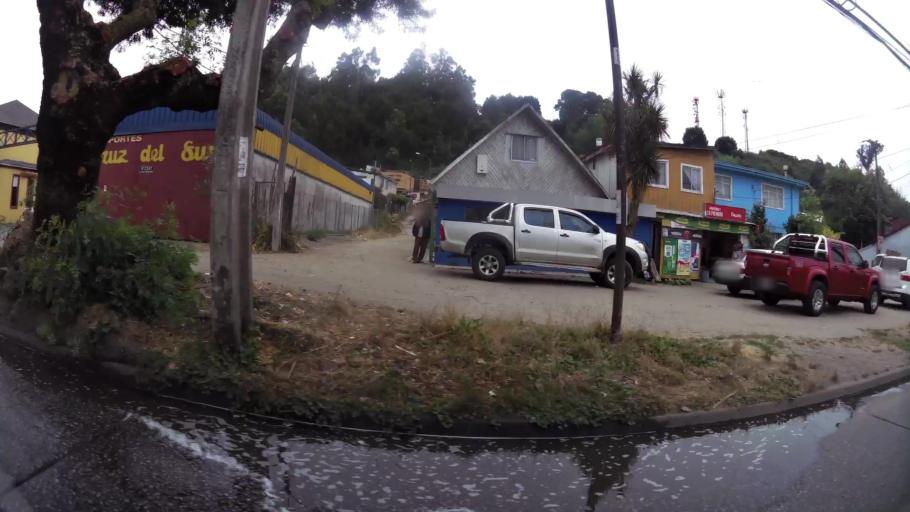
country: CL
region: Biobio
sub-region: Provincia de Concepcion
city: Concepcion
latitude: -36.8109
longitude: -73.0357
